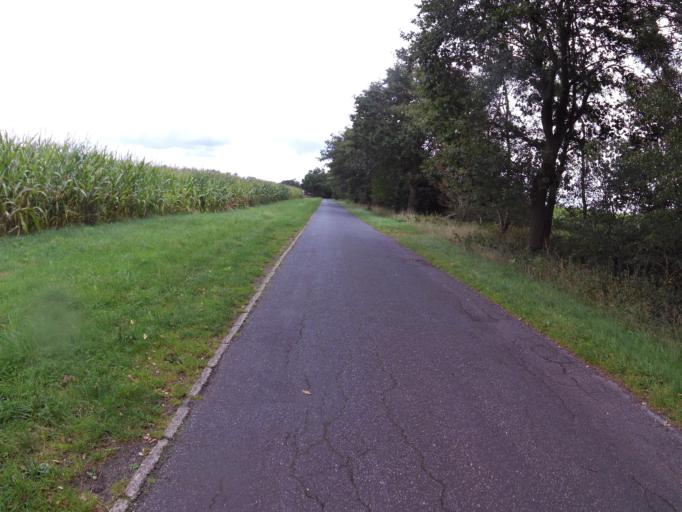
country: DE
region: Lower Saxony
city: Lunestedt
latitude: 53.5027
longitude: 8.7823
